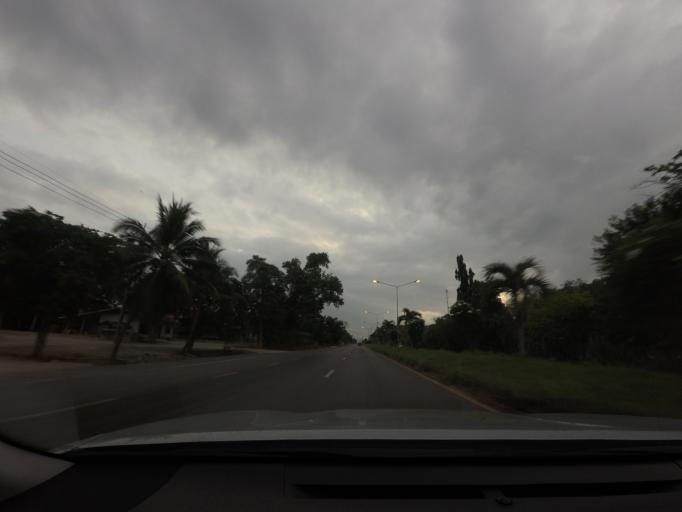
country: TH
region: Surat Thani
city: Khiri Ratthanikhom
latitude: 9.0387
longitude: 99.0800
